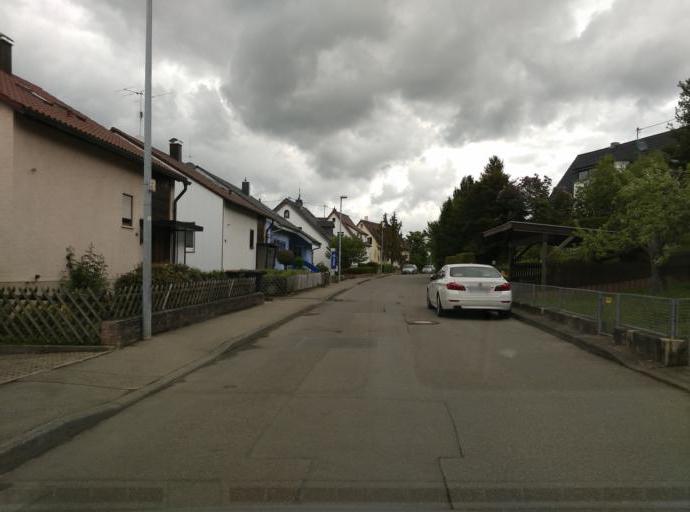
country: DE
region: Baden-Wuerttemberg
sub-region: Tuebingen Region
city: Wannweil
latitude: 48.5125
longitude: 9.1475
